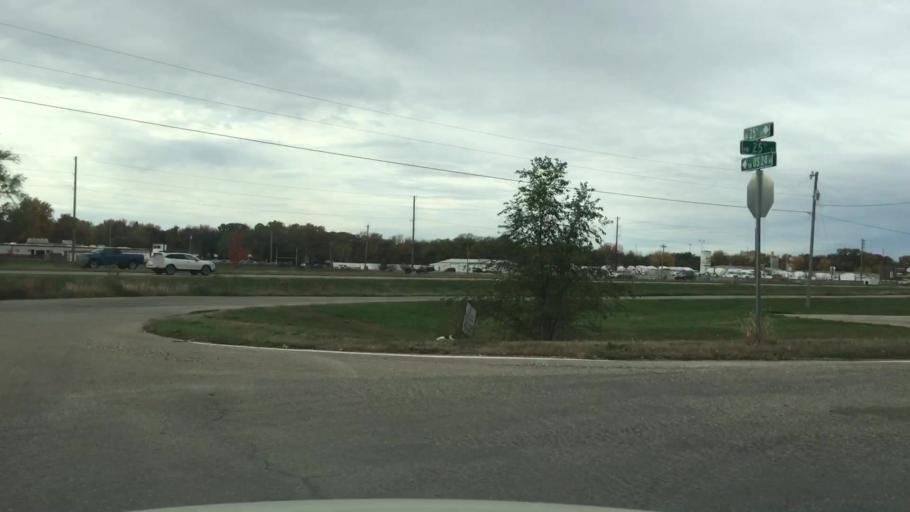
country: US
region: Kansas
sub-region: Shawnee County
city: Topeka
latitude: 39.0917
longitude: -95.6763
